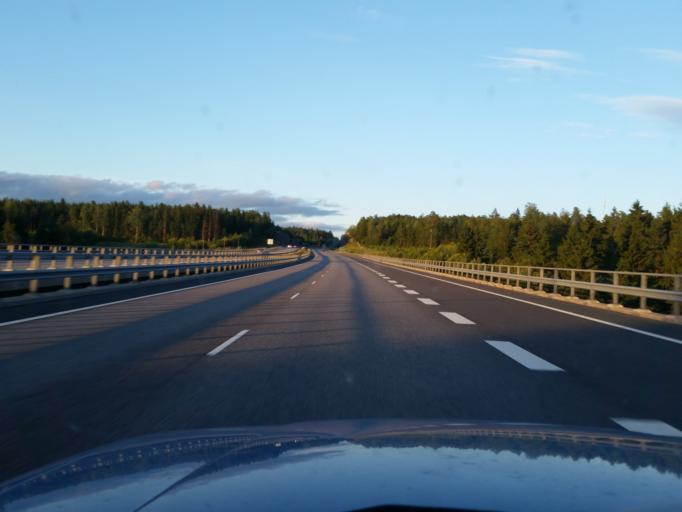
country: FI
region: Varsinais-Suomi
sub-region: Salo
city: Halikko
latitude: 60.4335
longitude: 22.9347
